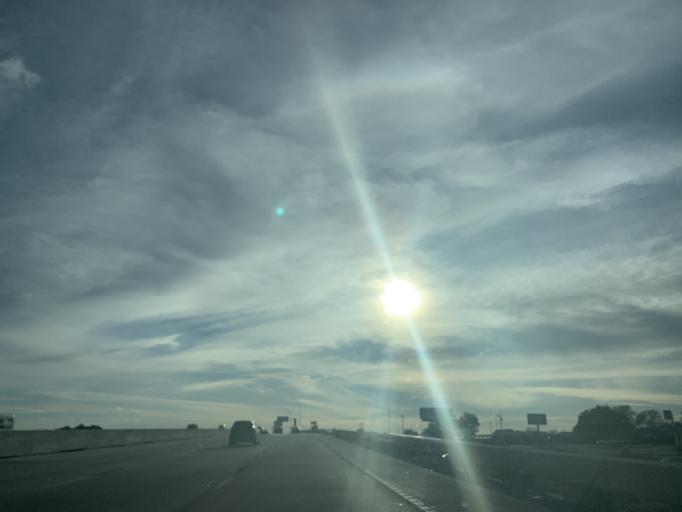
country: US
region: Texas
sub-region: Bell County
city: Salado
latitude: 30.9584
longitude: -97.5338
